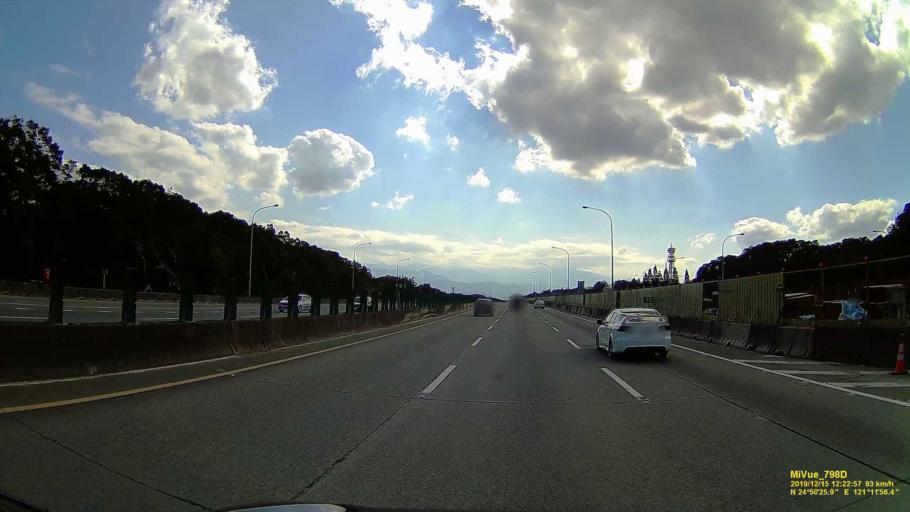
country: TW
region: Taiwan
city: Daxi
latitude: 24.8399
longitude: 121.1989
